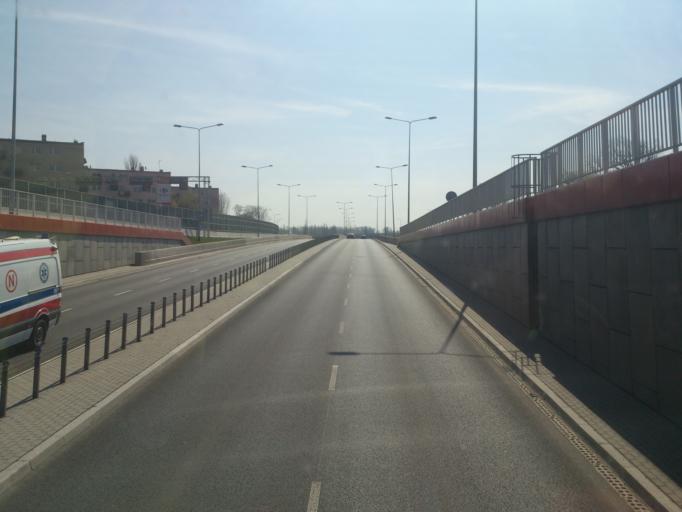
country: PL
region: Lodz Voivodeship
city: Lodz
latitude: 51.7263
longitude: 19.4483
